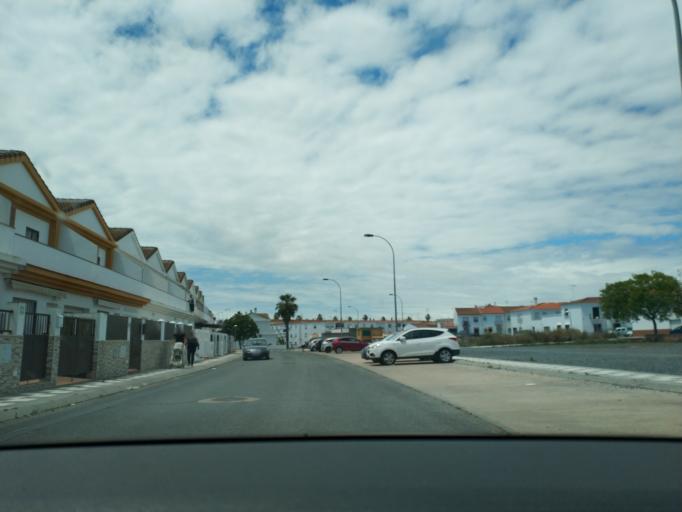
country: ES
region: Andalusia
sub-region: Provincia de Huelva
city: Cartaya
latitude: 37.2828
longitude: -7.1462
